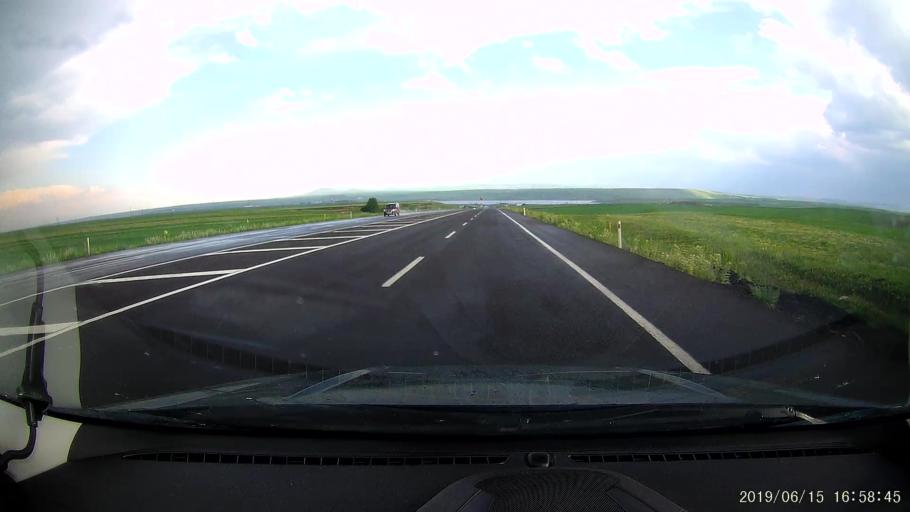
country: TR
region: Kars
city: Susuz
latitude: 40.7607
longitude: 43.1458
